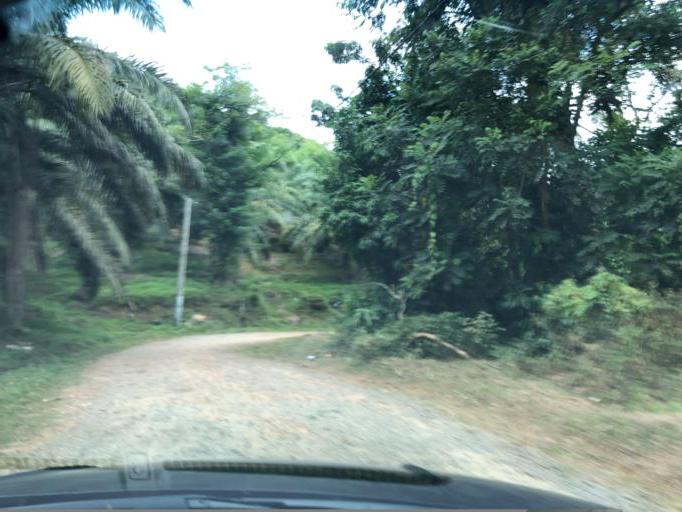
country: LK
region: Western
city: Horawala Junction
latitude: 6.5479
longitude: 80.0935
